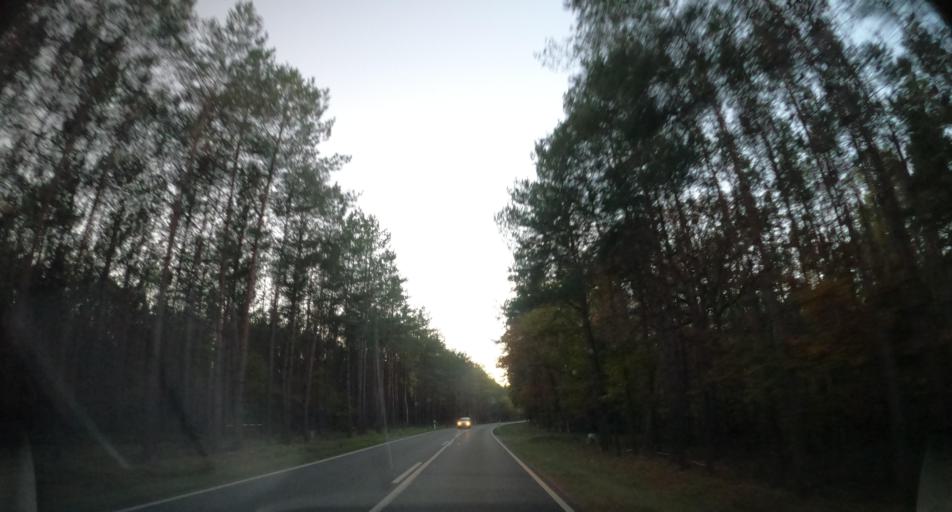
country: DE
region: Mecklenburg-Vorpommern
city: Ueckermunde
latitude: 53.7667
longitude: 13.9435
